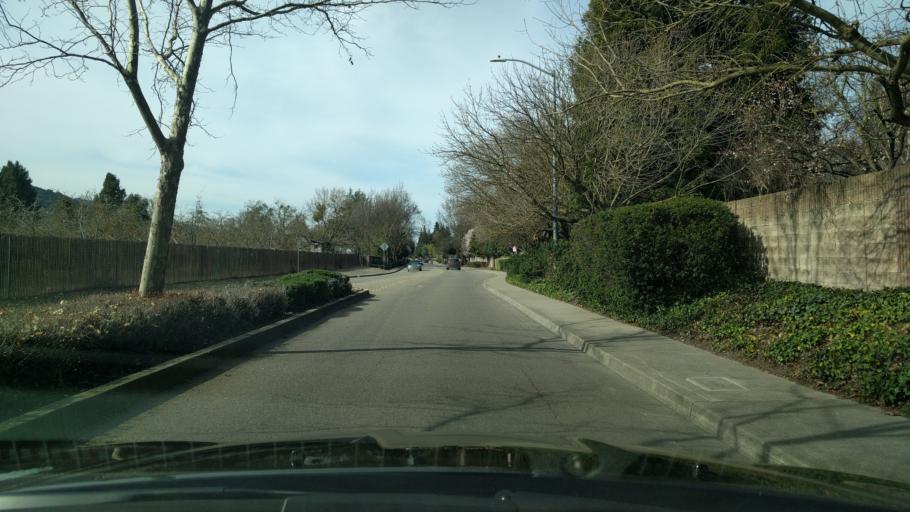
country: US
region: California
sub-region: Contra Costa County
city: San Ramon
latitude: 37.7837
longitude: -121.9757
